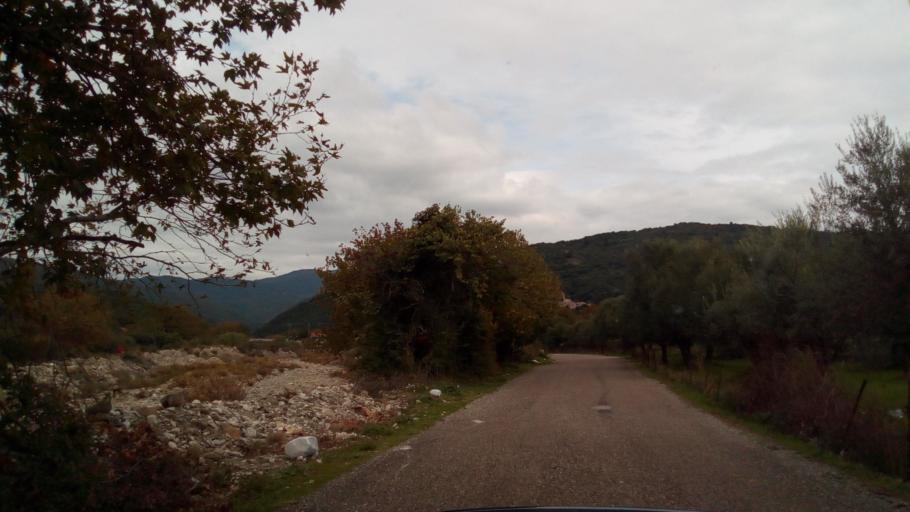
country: GR
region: West Greece
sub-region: Nomos Achaias
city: Kamarai
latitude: 38.4191
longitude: 21.9562
